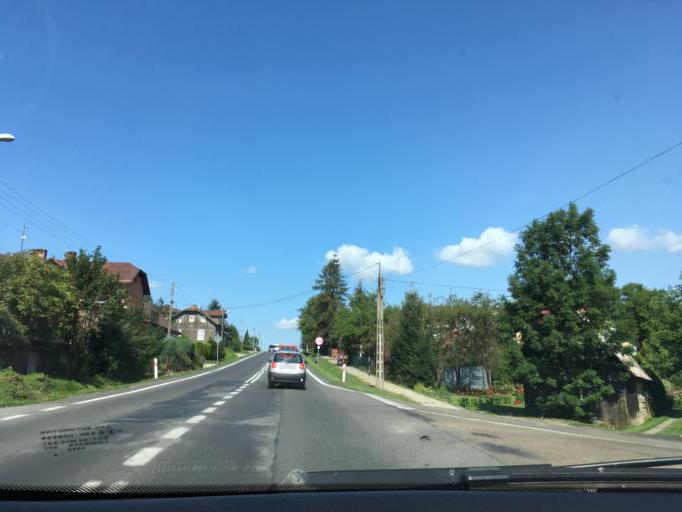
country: PL
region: Subcarpathian Voivodeship
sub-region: Powiat sanocki
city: Zagorz
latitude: 49.5199
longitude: 22.2578
